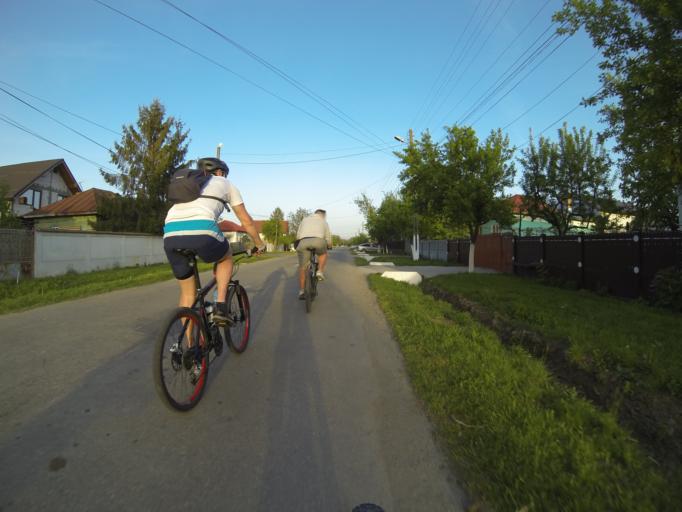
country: RO
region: Dolj
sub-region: Comuna Pielesti
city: Pielesti
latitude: 44.3457
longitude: 23.9281
